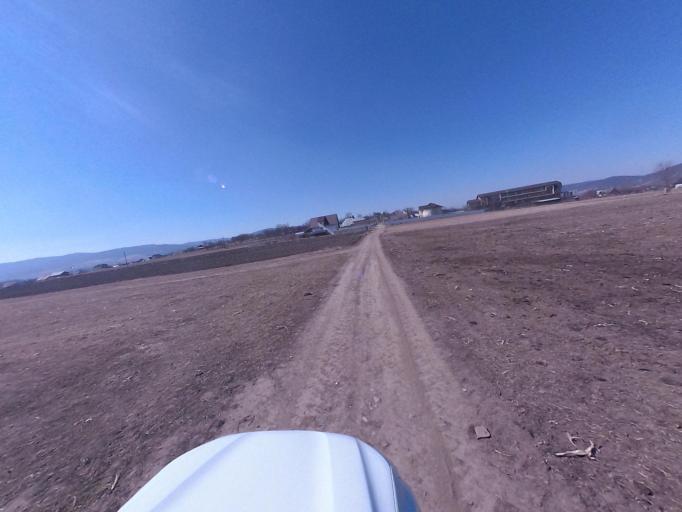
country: RO
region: Neamt
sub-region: Oras Targu Neamt
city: Humulesti
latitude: 47.1890
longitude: 26.3456
